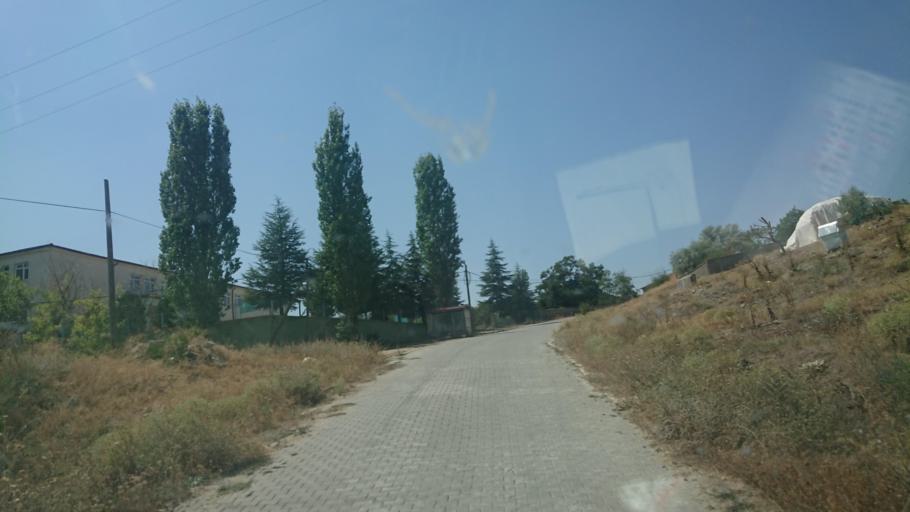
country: TR
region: Aksaray
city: Agacoren
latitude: 38.8190
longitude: 33.9565
